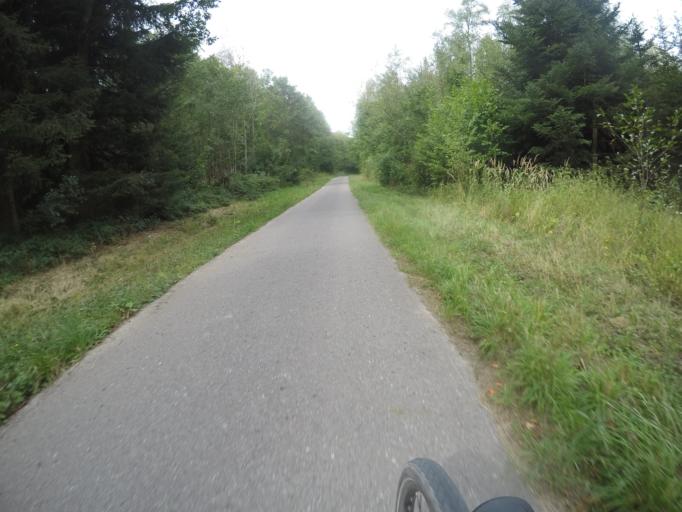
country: DE
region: Baden-Wuerttemberg
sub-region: Karlsruhe Region
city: Wurmberg
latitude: 48.8672
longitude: 8.7830
